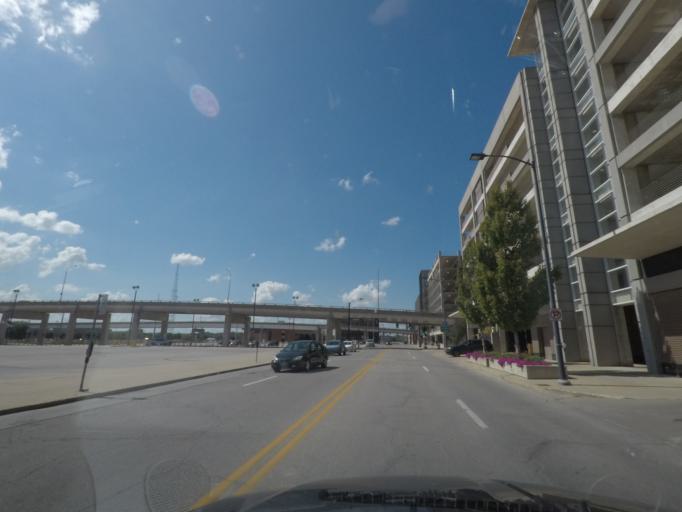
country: US
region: Iowa
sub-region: Polk County
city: Des Moines
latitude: 41.5838
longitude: -93.6255
